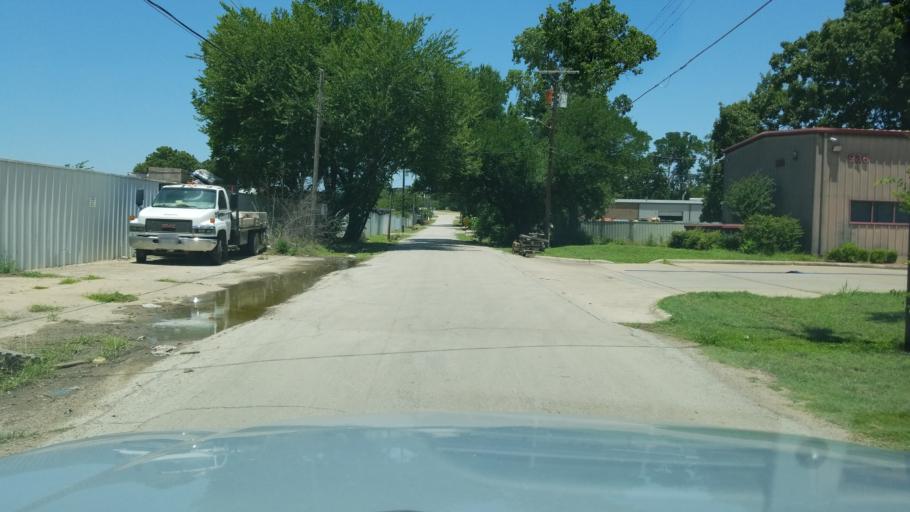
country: US
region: Texas
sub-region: Dallas County
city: Irving
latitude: 32.8033
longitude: -96.9207
